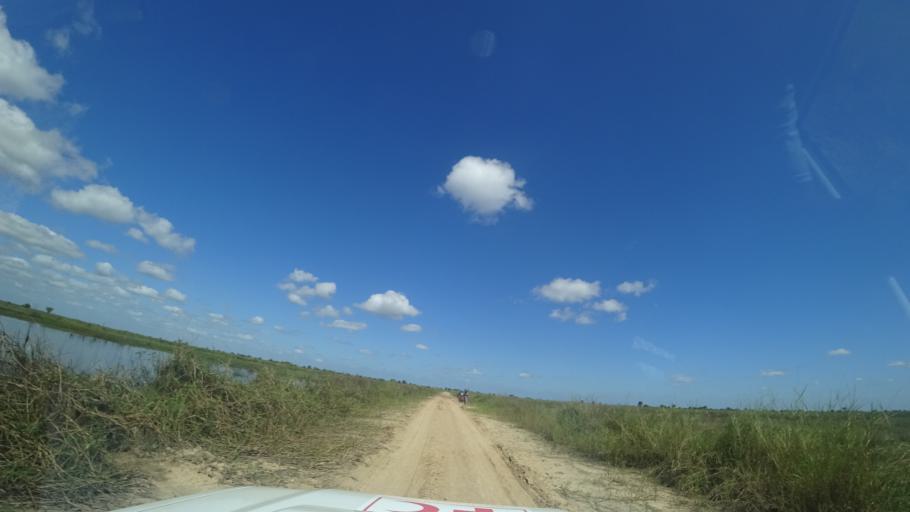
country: MZ
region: Sofala
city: Dondo
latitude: -19.3950
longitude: 34.5731
